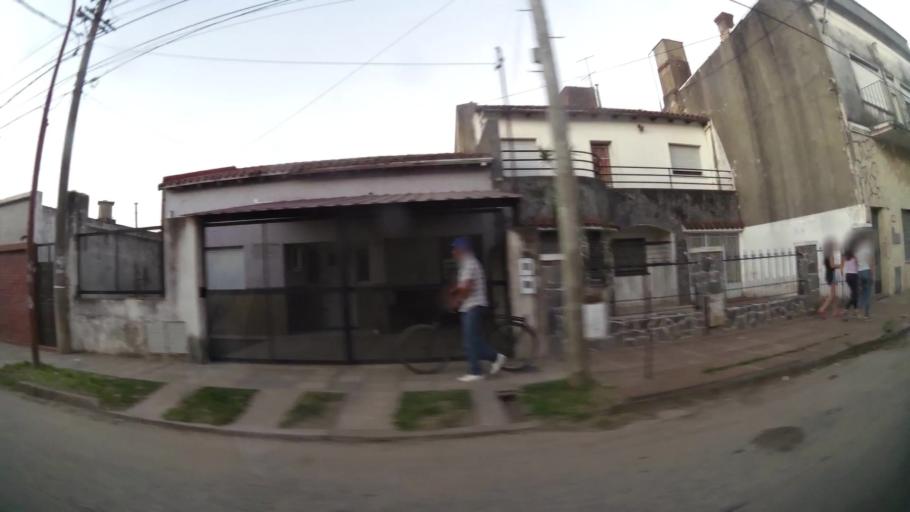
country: AR
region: Santa Fe
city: Santa Fe de la Vera Cruz
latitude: -31.6030
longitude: -60.7057
